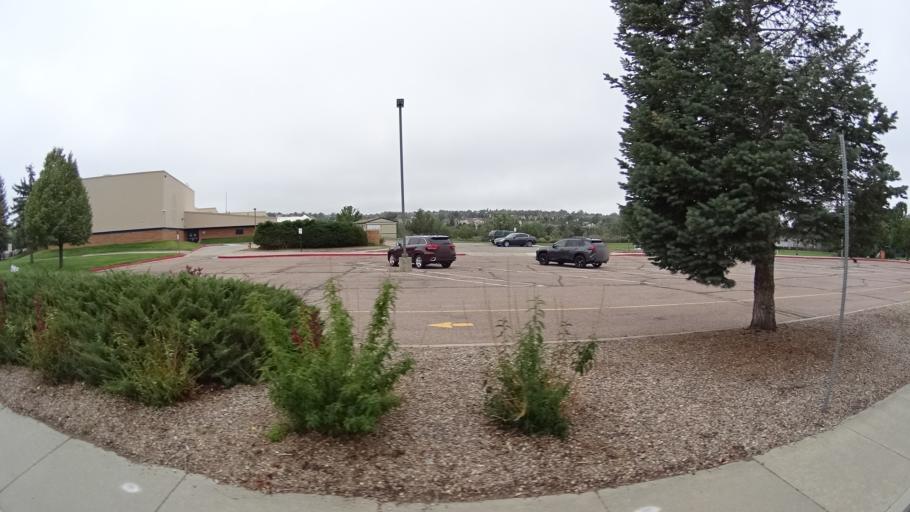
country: US
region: Colorado
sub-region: El Paso County
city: Cimarron Hills
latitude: 38.9325
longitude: -104.7581
